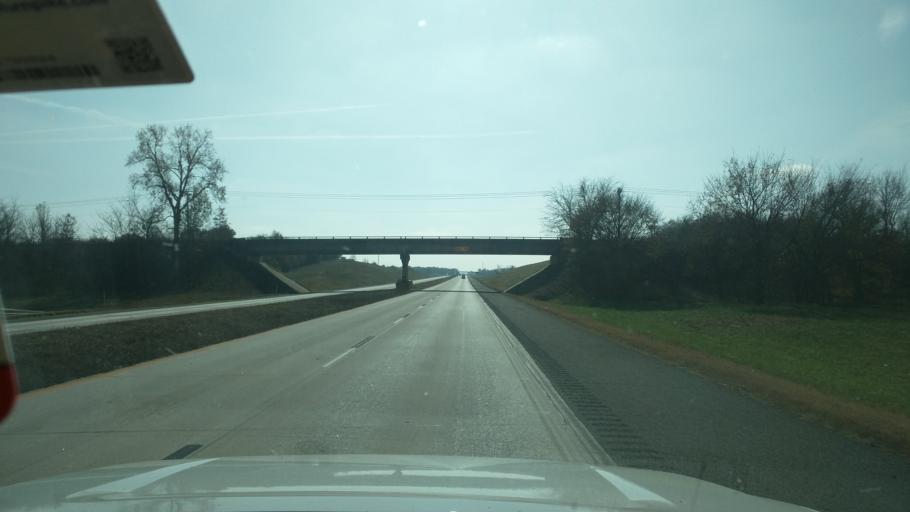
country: US
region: Oklahoma
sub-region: Muskogee County
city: Muskogee
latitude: 35.7127
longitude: -95.3098
